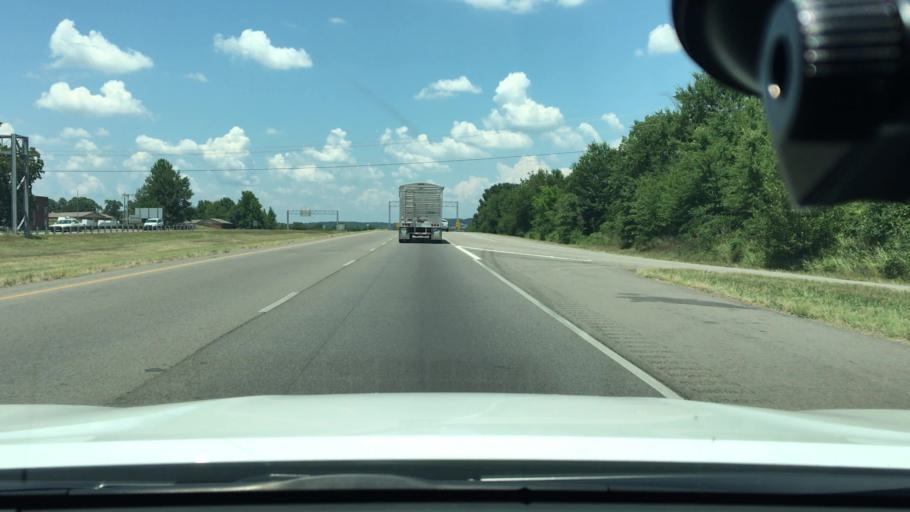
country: US
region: Arkansas
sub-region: Crawford County
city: Van Buren
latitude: 35.4500
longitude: -94.3202
